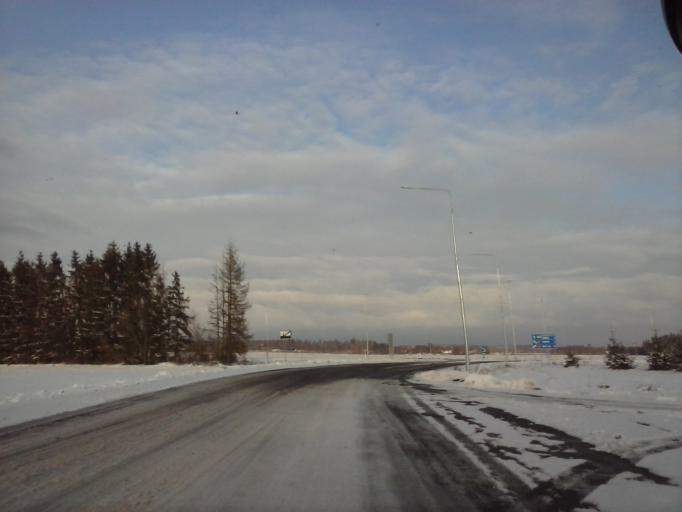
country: EE
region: Tartu
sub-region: Tartu linn
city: Tartu
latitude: 58.3599
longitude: 26.8909
